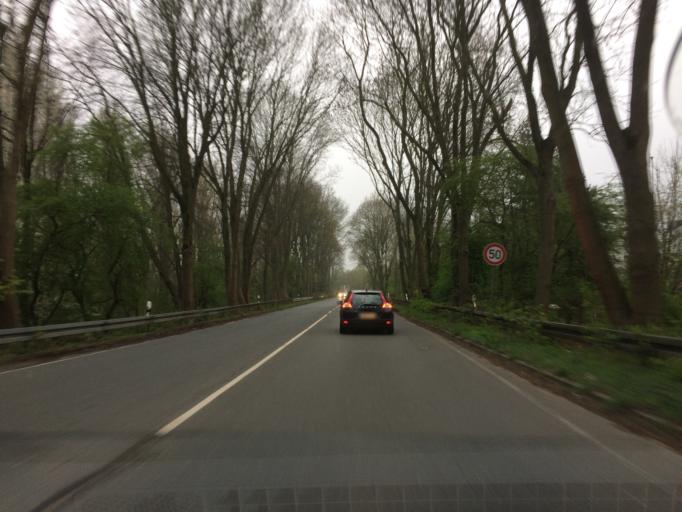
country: DE
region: North Rhine-Westphalia
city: Hattingen
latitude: 51.4339
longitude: 7.1776
